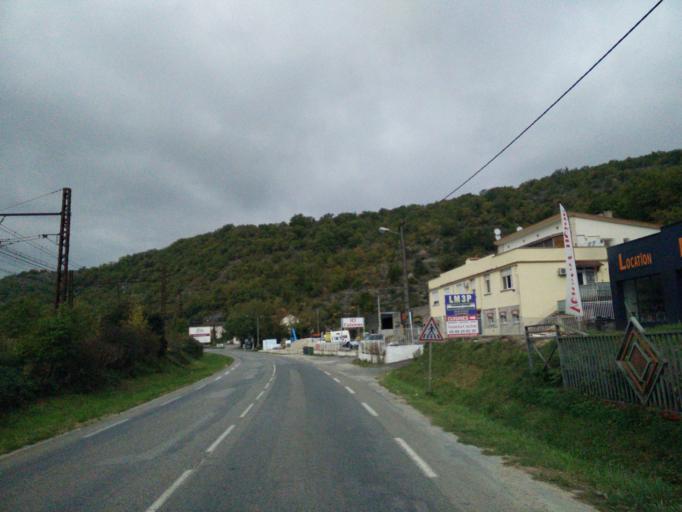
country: FR
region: Midi-Pyrenees
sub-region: Departement du Lot
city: Cahors
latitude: 44.4751
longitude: 1.4282
